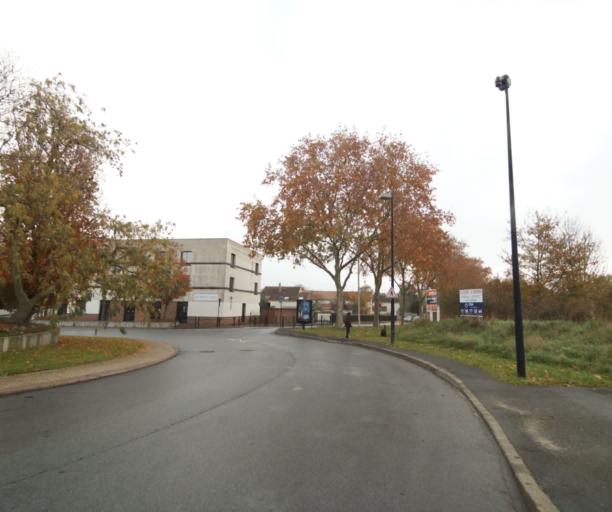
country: FR
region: Ile-de-France
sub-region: Departement de l'Essonne
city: Lisses
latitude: 48.6140
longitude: 2.4341
